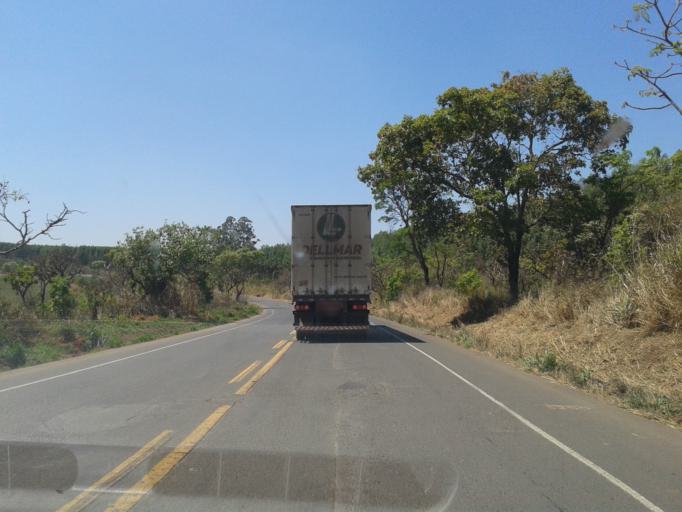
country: BR
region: Minas Gerais
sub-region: Araxa
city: Araxa
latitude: -19.4359
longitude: -47.2134
